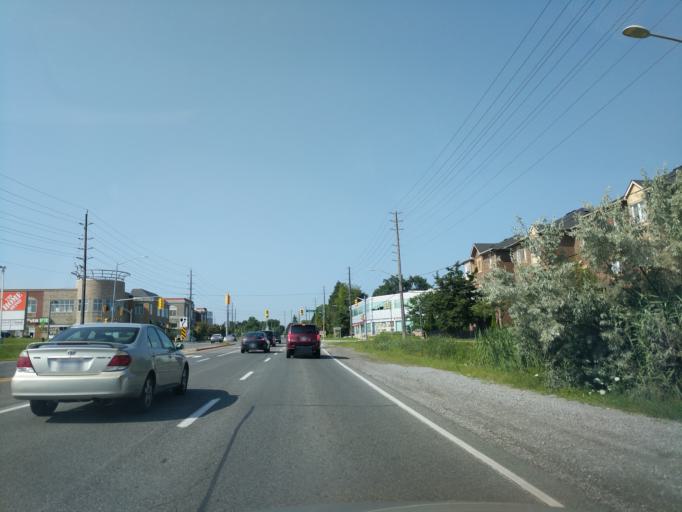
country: CA
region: Ontario
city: Ajax
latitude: 43.8317
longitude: -79.0958
